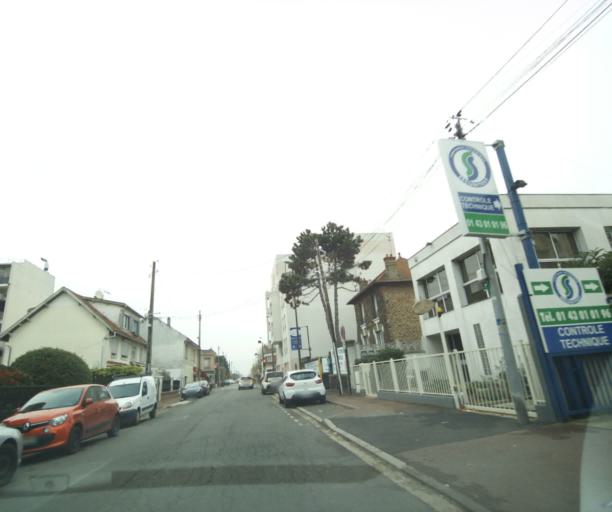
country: FR
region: Ile-de-France
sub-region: Departement de Seine-Saint-Denis
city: Le Raincy
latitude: 48.9124
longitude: 2.5179
